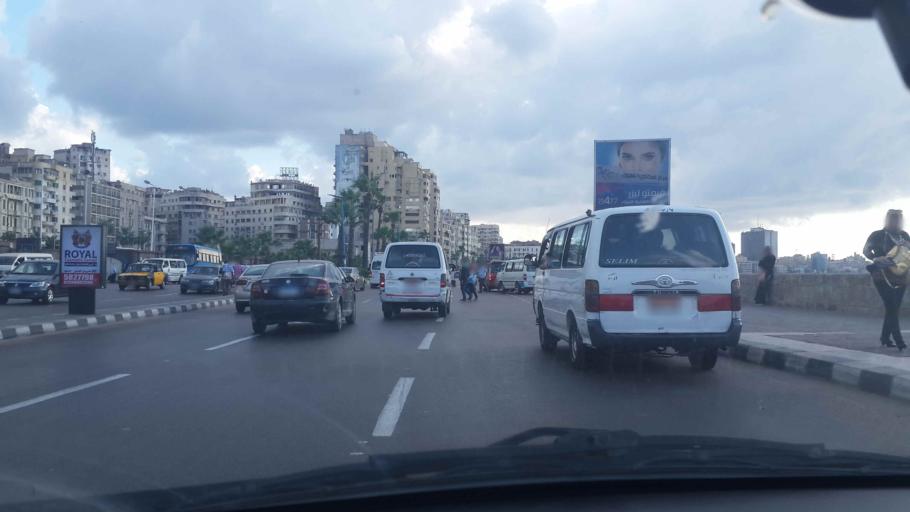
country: EG
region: Alexandria
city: Alexandria
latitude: 31.2086
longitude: 29.9071
